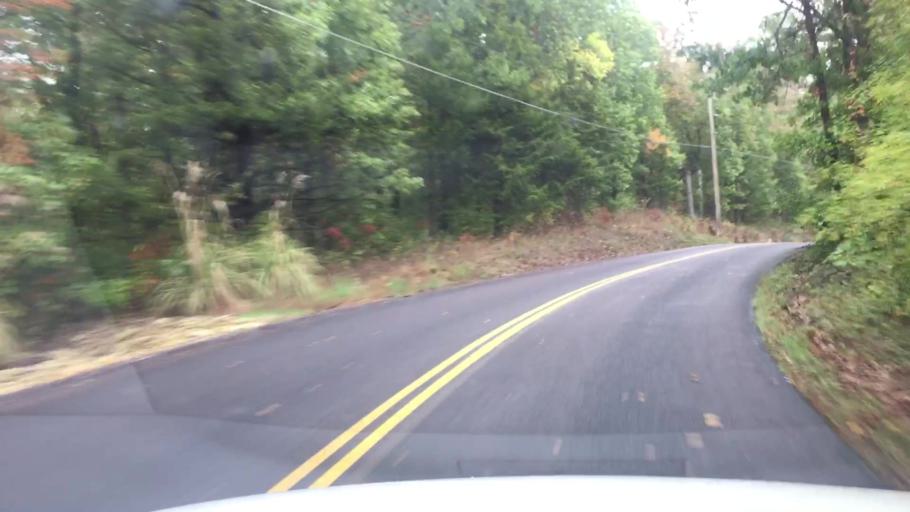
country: US
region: Missouri
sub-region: Boone County
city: Columbia
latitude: 38.8587
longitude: -92.3481
